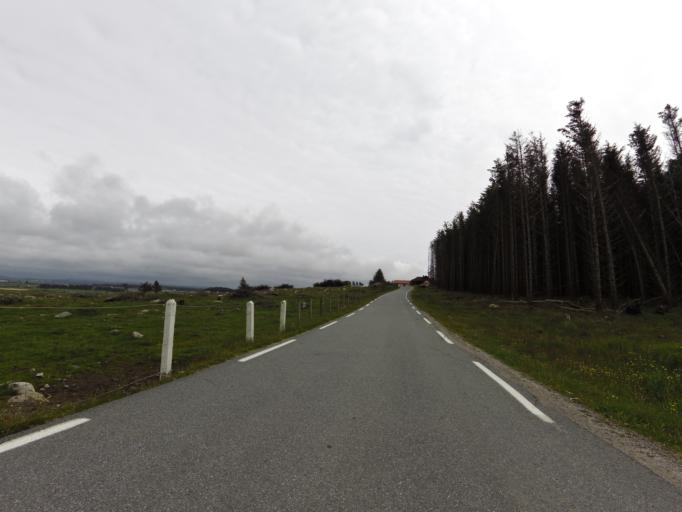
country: NO
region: Rogaland
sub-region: Ha
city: Naerbo
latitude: 58.6613
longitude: 5.5583
